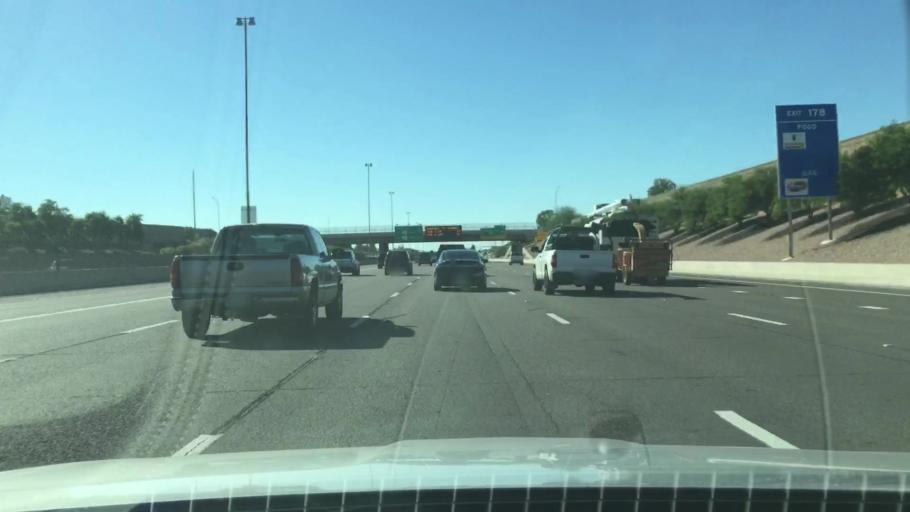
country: US
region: Arizona
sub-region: Maricopa County
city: San Carlos
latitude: 33.3867
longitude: -111.8464
